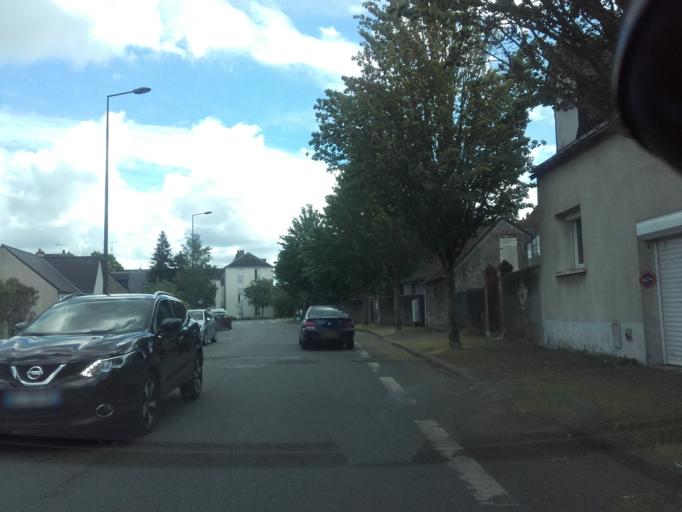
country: FR
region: Centre
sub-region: Departement d'Indre-et-Loire
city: Saint-Cyr-sur-Loire
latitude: 47.4268
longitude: 0.6892
